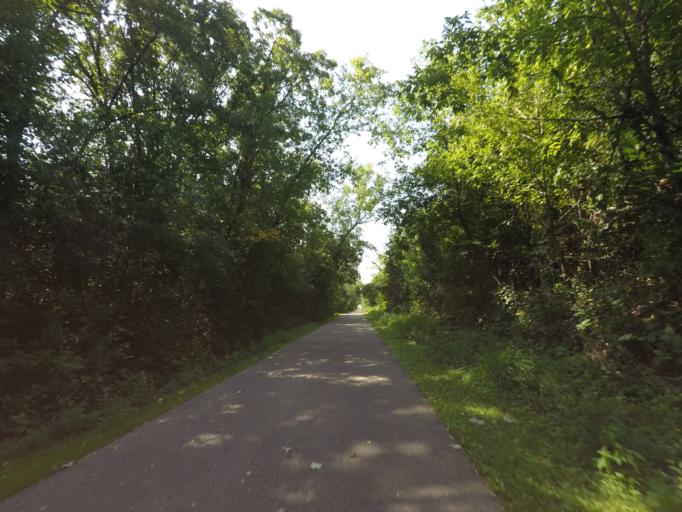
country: US
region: Wisconsin
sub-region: Jefferson County
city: Fort Atkinson
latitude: 42.8948
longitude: -88.8658
